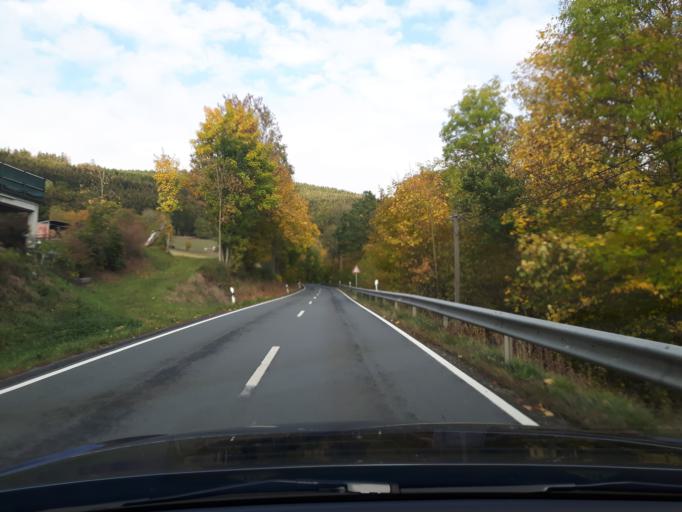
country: DE
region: North Rhine-Westphalia
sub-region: Regierungsbezirk Arnsberg
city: Bad Berleburg
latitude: 51.0166
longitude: 8.4394
